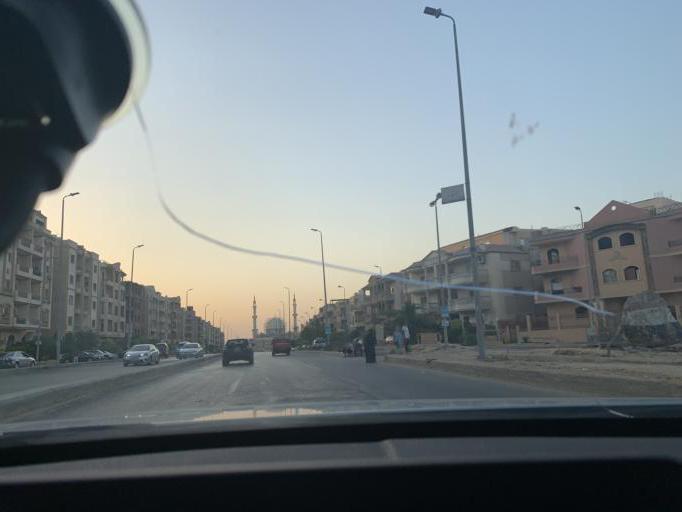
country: EG
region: Muhafazat al Qahirah
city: Cairo
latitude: 30.0019
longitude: 31.4609
